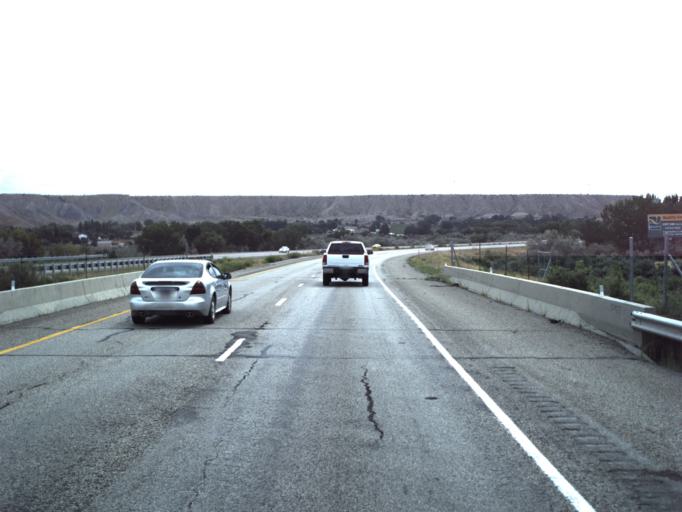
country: US
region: Utah
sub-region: Carbon County
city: Carbonville
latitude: 39.6159
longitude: -110.8446
